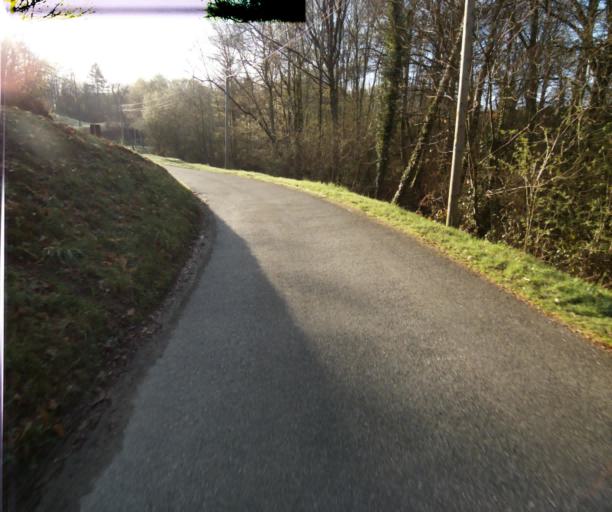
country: FR
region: Limousin
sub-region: Departement de la Correze
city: Correze
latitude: 45.2939
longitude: 1.8487
